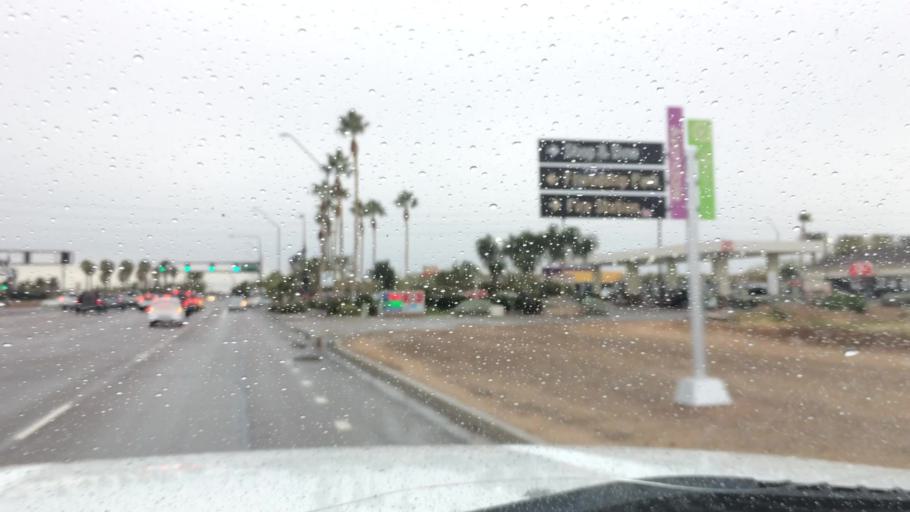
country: US
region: Arizona
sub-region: Maricopa County
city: Tolleson
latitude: 33.4629
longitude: -112.3065
